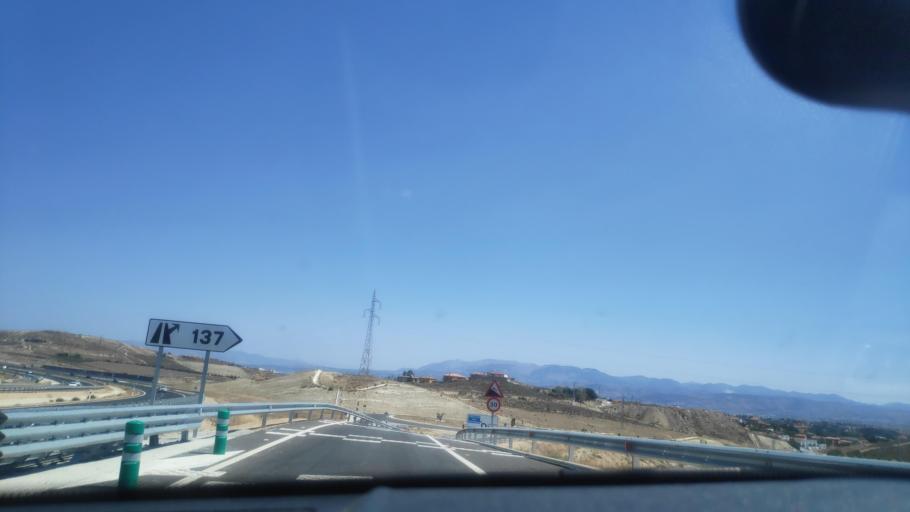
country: ES
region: Andalusia
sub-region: Provincia de Granada
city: Alhendin
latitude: 37.1009
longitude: -3.6727
